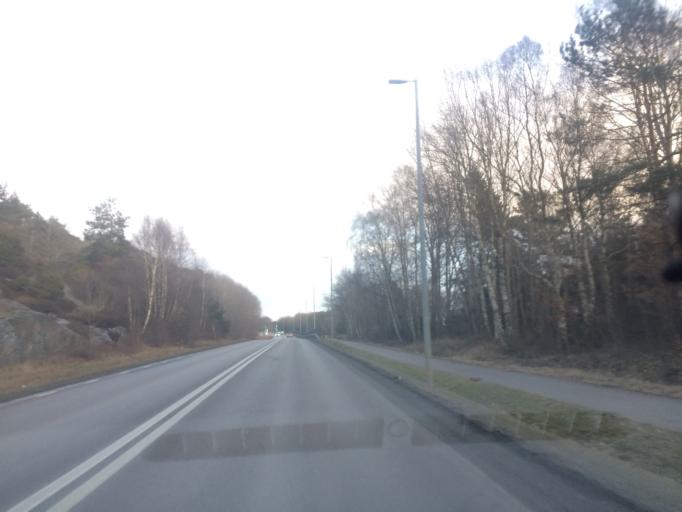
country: SE
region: Vaestra Goetaland
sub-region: Goteborg
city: Andalen
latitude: 57.7096
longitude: 11.7384
